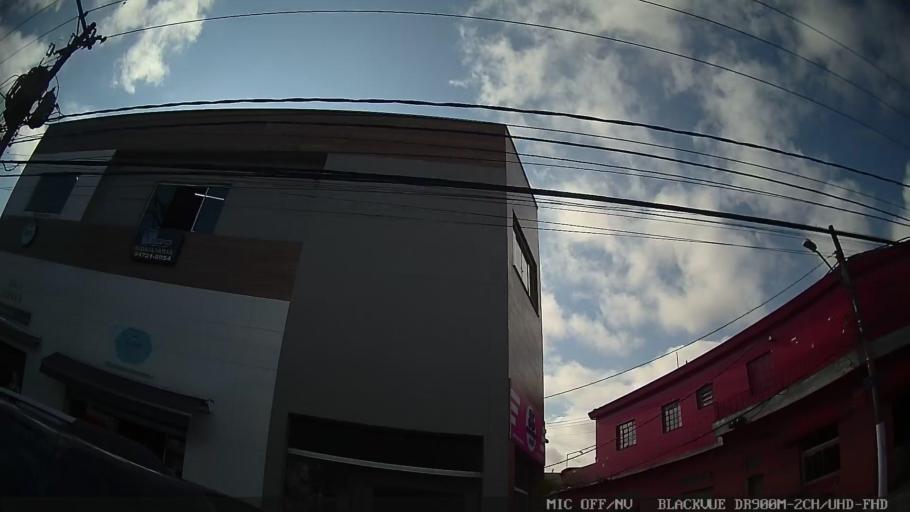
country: BR
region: Sao Paulo
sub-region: Guarulhos
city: Guarulhos
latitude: -23.5421
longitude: -46.4924
